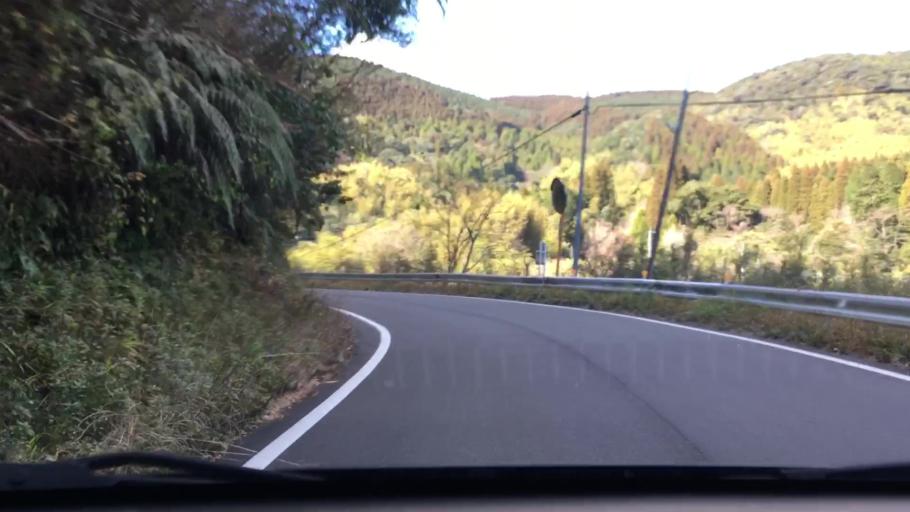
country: JP
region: Kagoshima
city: Ijuin
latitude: 31.7170
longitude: 130.4322
